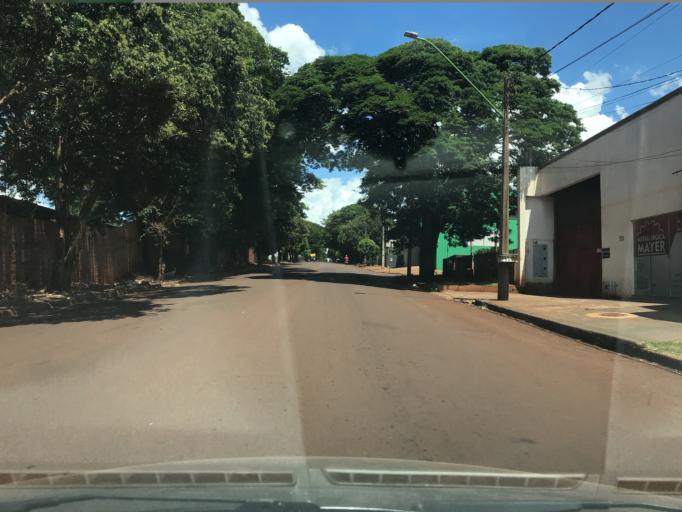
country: BR
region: Parana
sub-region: Palotina
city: Palotina
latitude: -24.2819
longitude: -53.8478
